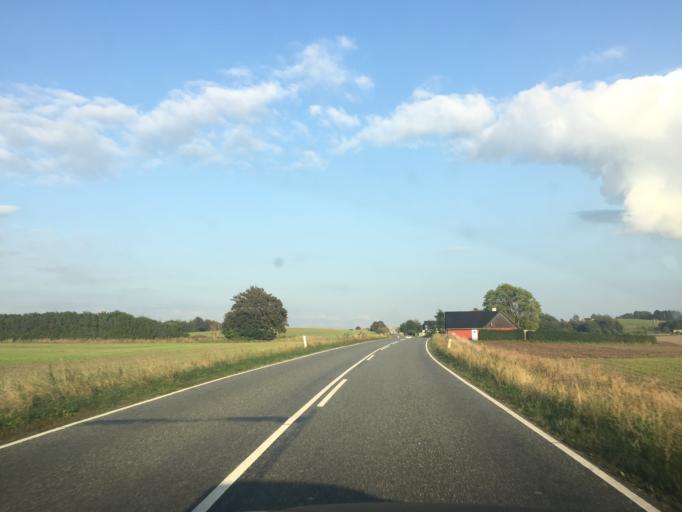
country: DK
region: Zealand
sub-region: Kalundborg Kommune
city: Hong
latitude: 55.5479
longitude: 11.3309
